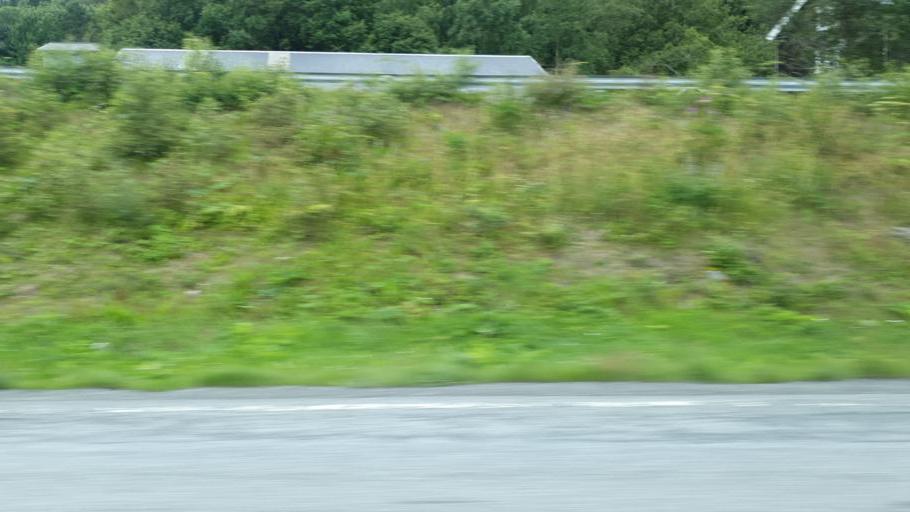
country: NO
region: Sor-Trondelag
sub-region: Midtre Gauldal
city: Storen
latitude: 63.0137
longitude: 10.2467
